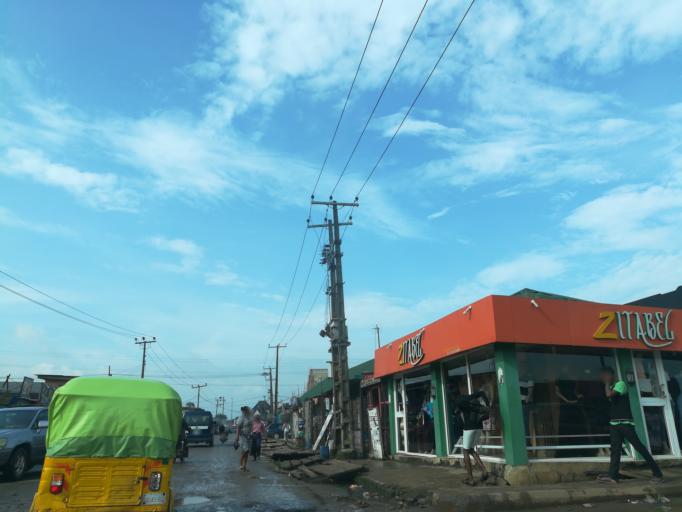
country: NG
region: Lagos
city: Ojota
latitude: 6.6076
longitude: 3.4220
